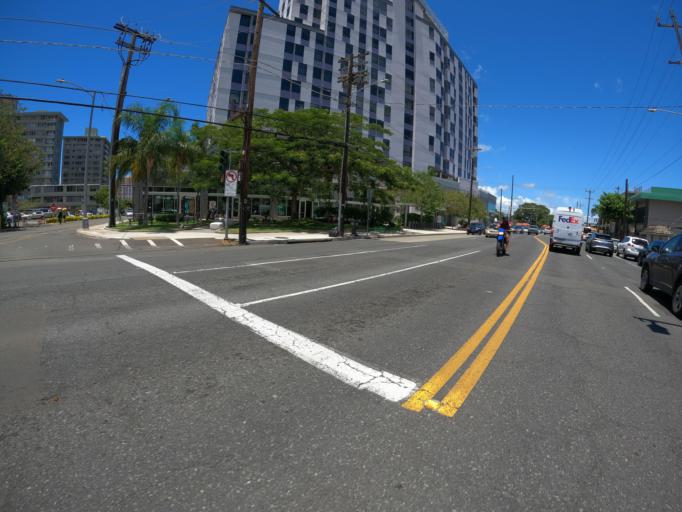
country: US
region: Hawaii
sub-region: Honolulu County
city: Honolulu
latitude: 21.2914
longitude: -157.8210
